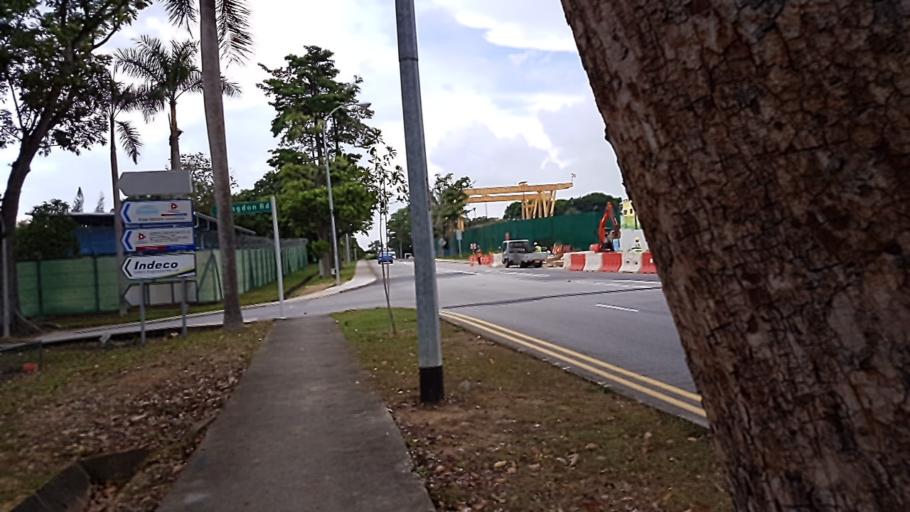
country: MY
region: Johor
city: Kampung Pasir Gudang Baru
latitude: 1.3695
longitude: 103.9791
